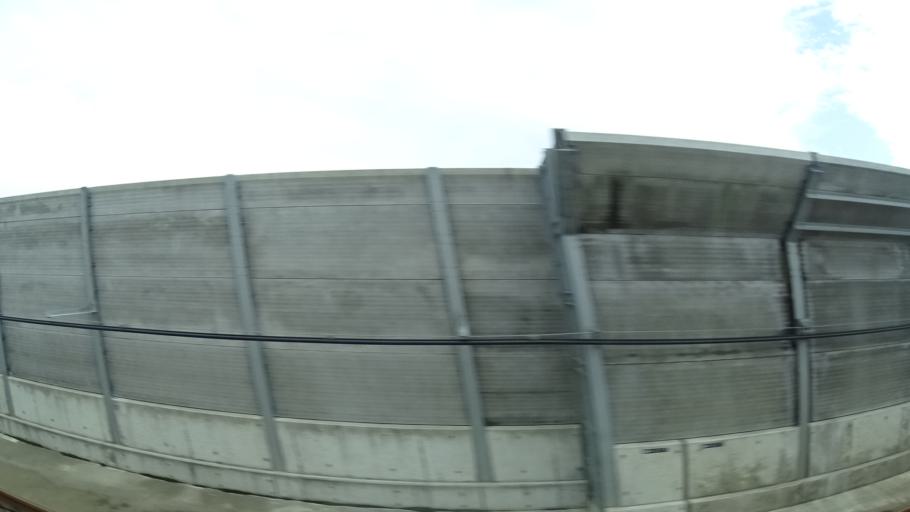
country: JP
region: Toyama
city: Nishishinminato
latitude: 36.7247
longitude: 137.0764
